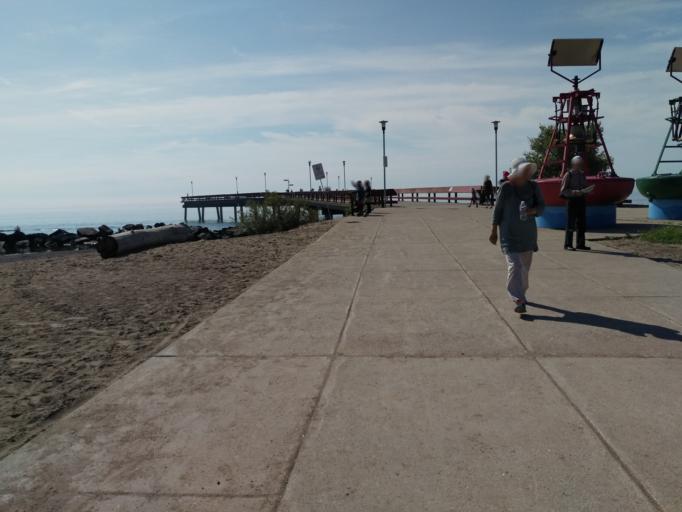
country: CA
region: Ontario
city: Toronto
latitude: 43.6167
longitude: -79.3719
